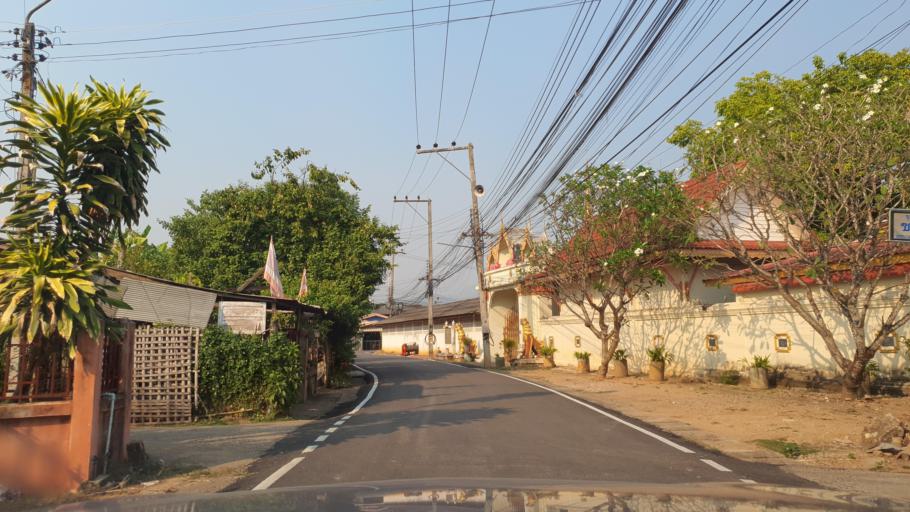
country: TH
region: Chiang Mai
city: Mae Taeng
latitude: 19.1438
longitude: 99.0114
